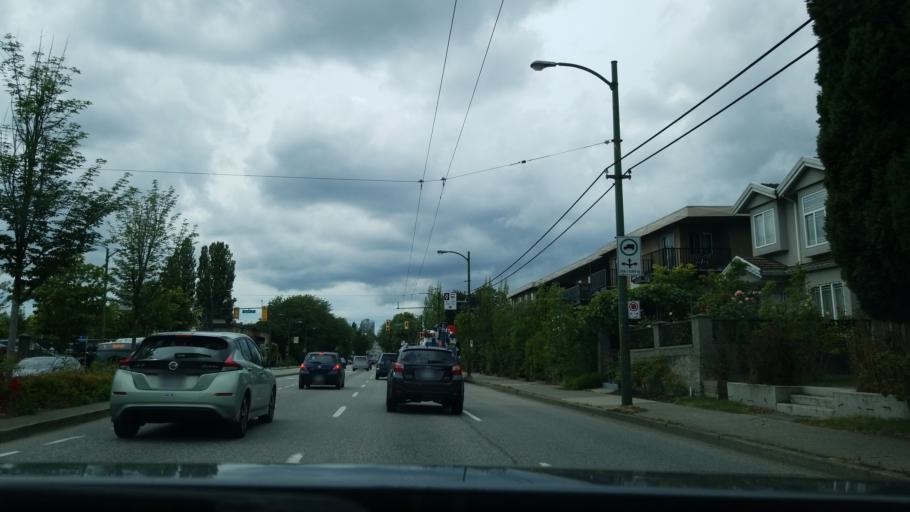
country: CA
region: British Columbia
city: Vancouver
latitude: 49.2624
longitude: -123.0761
